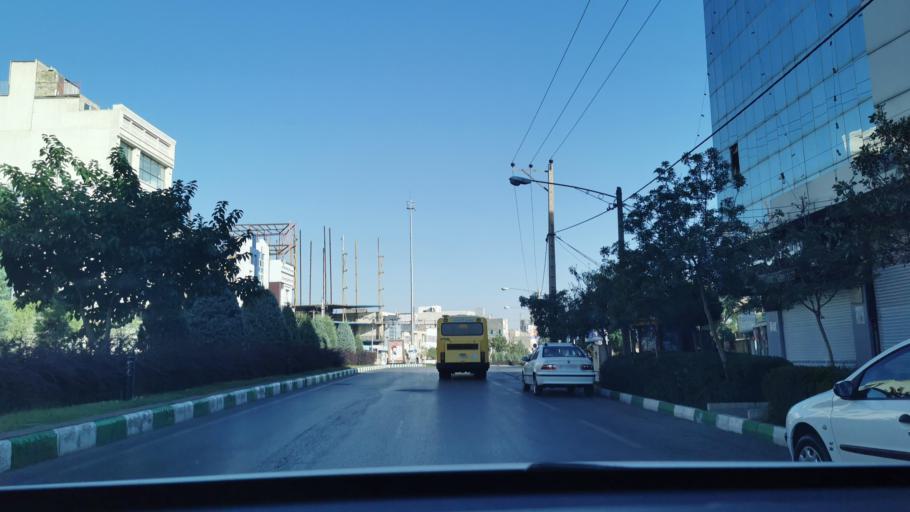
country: IR
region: Razavi Khorasan
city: Mashhad
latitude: 36.3064
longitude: 59.5098
